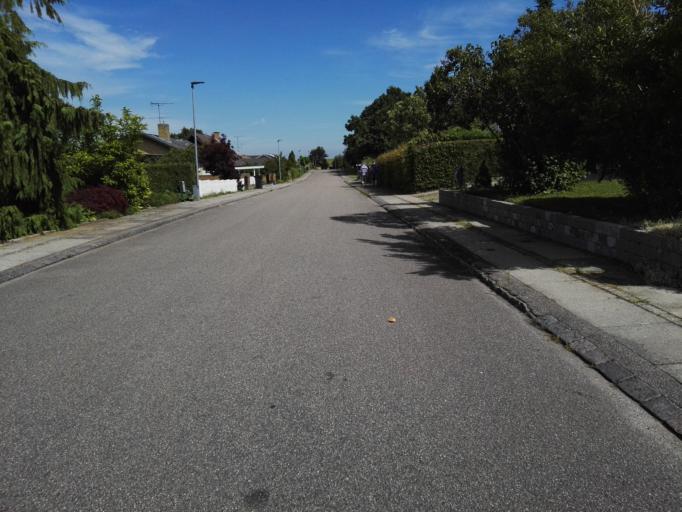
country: DK
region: Capital Region
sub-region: Egedal Kommune
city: Olstykke
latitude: 55.7956
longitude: 12.1477
